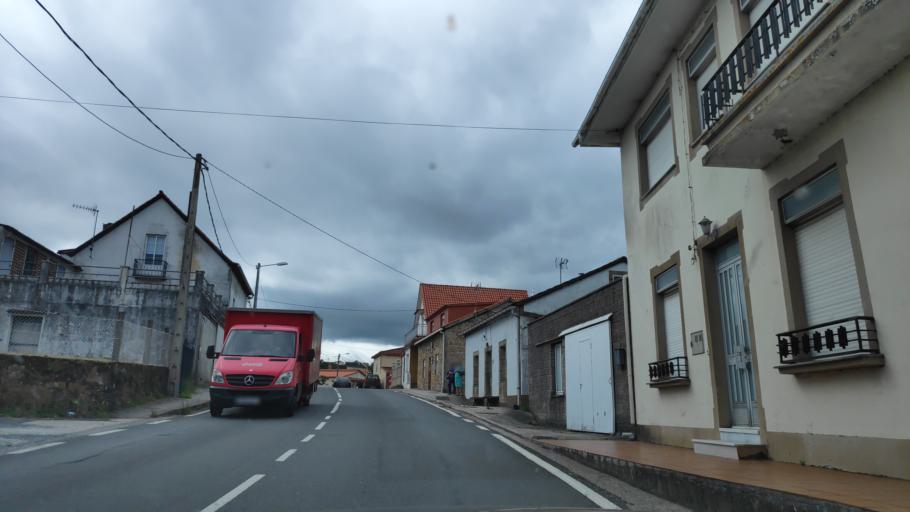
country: ES
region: Galicia
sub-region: Provincia da Coruna
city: Rianxo
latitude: 42.6698
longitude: -8.8142
